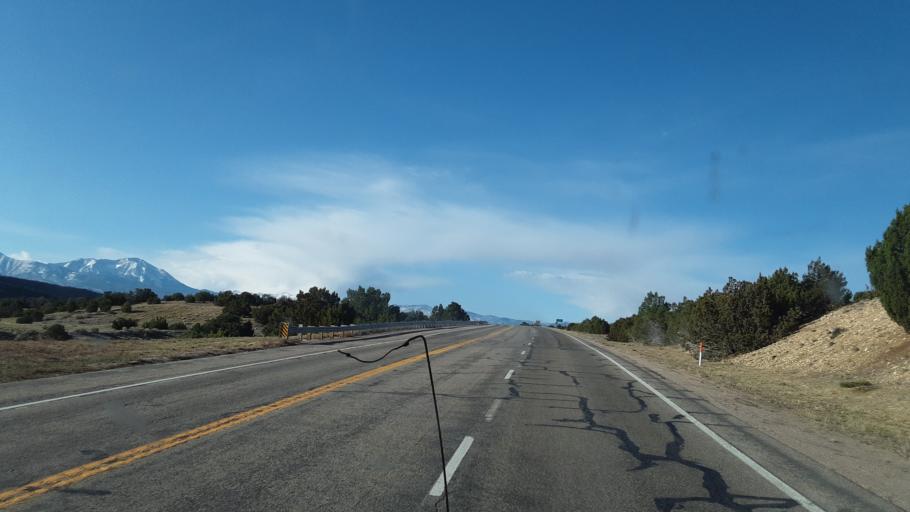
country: US
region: Colorado
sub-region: Huerfano County
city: Walsenburg
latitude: 37.6063
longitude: -104.8233
